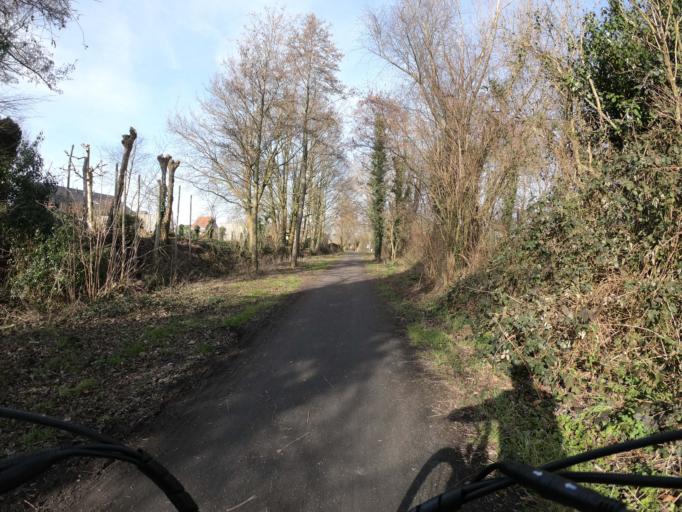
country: BE
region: Flanders
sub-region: Provincie West-Vlaanderen
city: Ledegem
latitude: 50.8357
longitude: 3.1233
